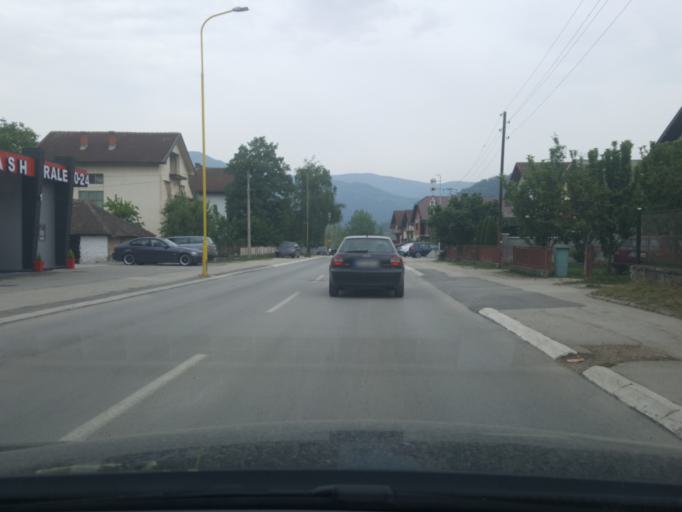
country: RS
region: Central Serbia
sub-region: Zlatiborski Okrug
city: Bajina Basta
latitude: 43.9762
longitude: 19.5690
